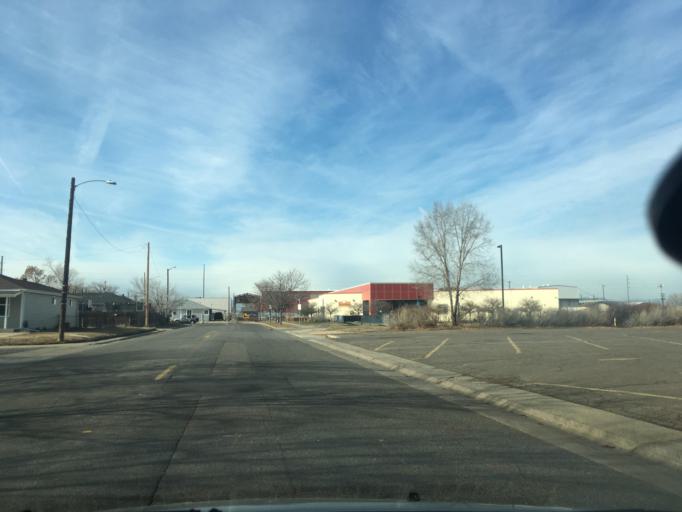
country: US
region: Colorado
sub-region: Adams County
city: Commerce City
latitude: 39.7838
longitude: -104.9558
